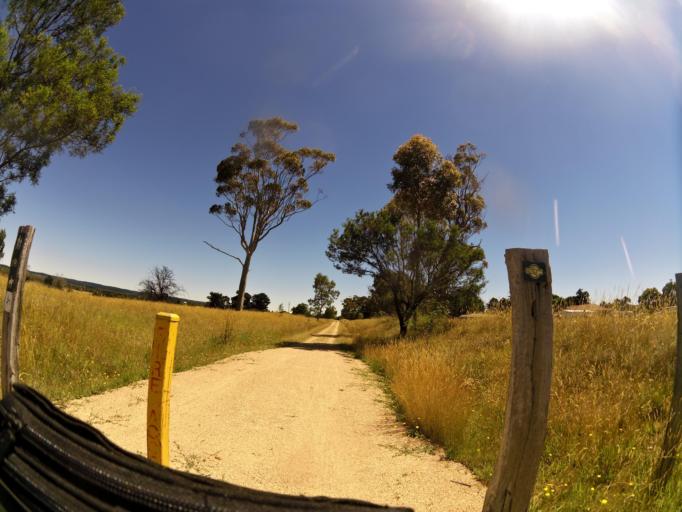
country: AU
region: Victoria
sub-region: Ballarat North
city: Delacombe
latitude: -37.6929
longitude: 143.6545
